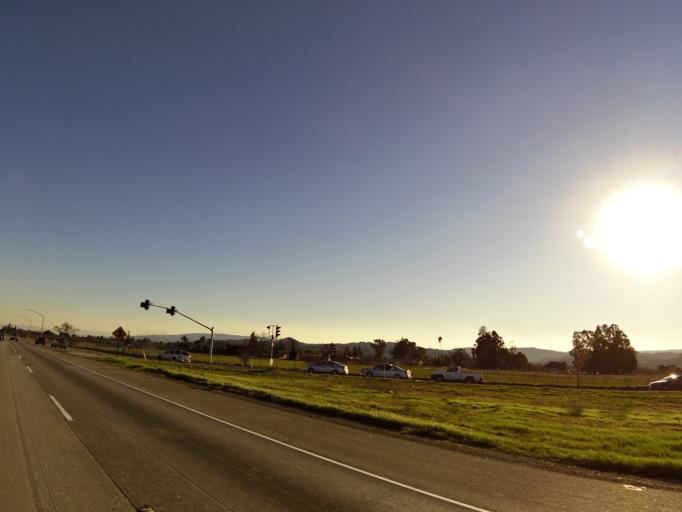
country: US
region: California
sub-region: Santa Clara County
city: Morgan Hill
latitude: 37.1183
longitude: -121.6259
